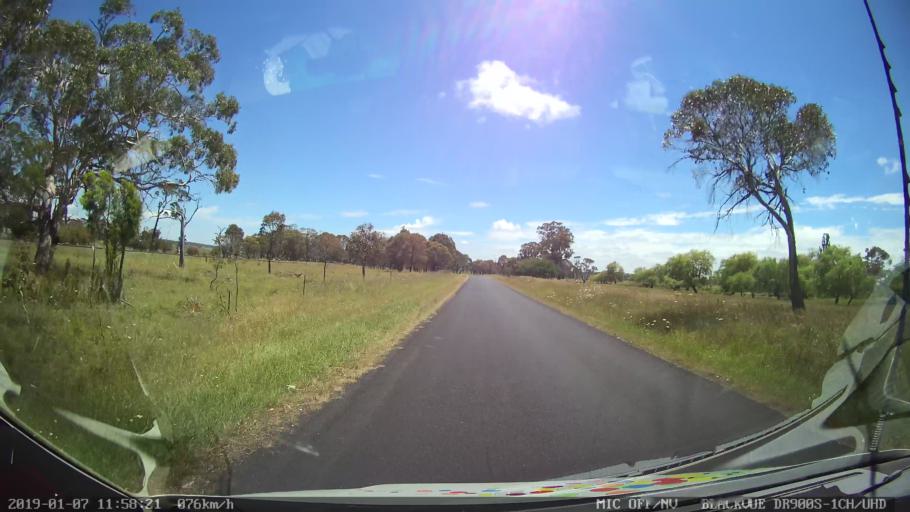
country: AU
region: New South Wales
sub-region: Guyra
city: Guyra
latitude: -30.2544
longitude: 151.6674
